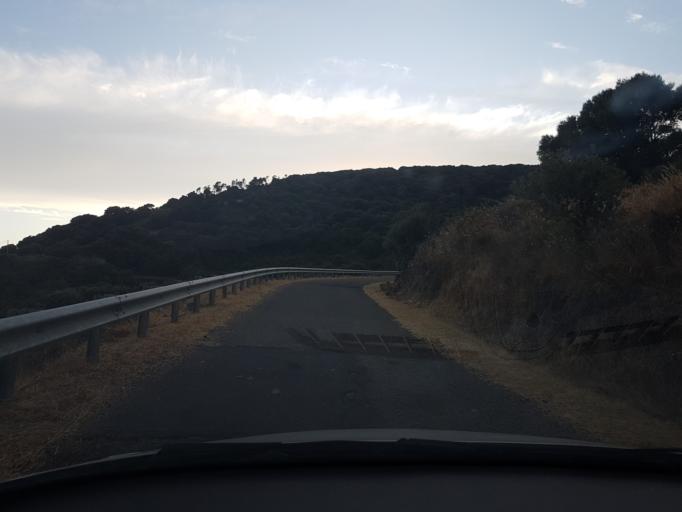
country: IT
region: Sardinia
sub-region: Provincia di Oristano
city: Seneghe
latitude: 40.1102
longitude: 8.6093
